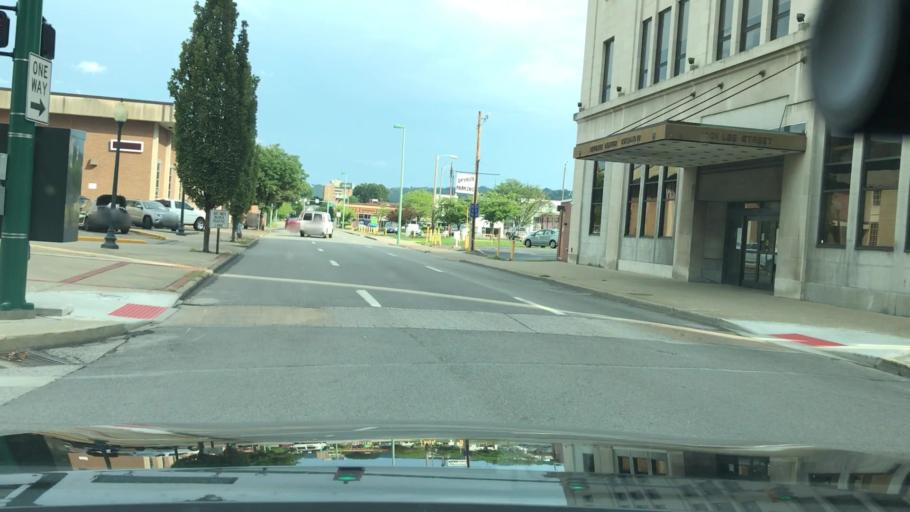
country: US
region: West Virginia
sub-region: Kanawha County
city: Charleston
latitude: 38.3498
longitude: -81.6325
